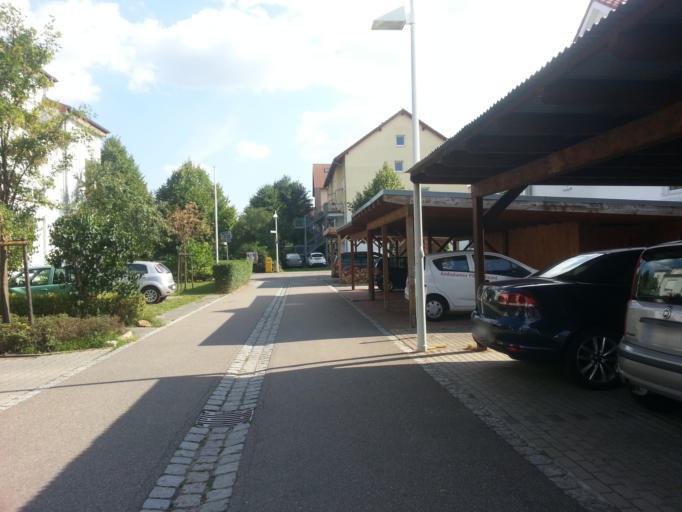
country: DE
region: Baden-Wuerttemberg
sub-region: Karlsruhe Region
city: Schriesheim
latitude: 49.4711
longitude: 8.6519
